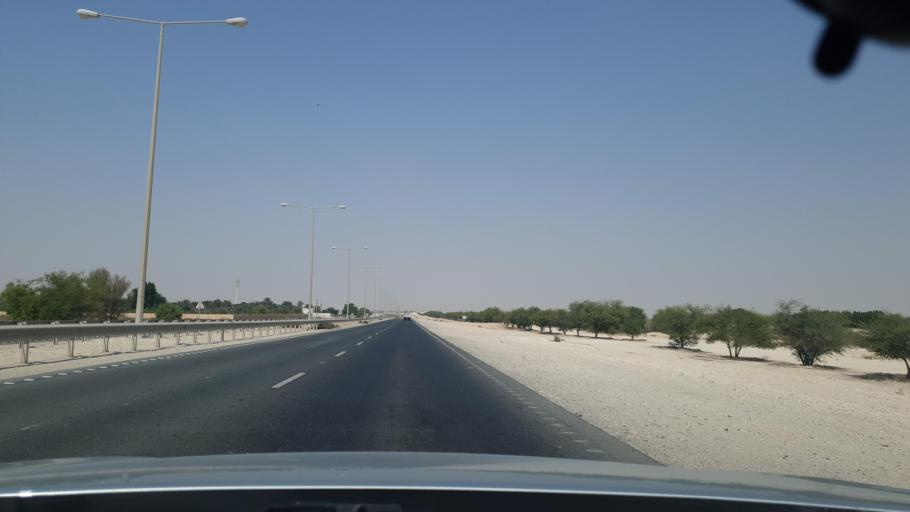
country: QA
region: Al Khawr
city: Al Khawr
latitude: 25.7255
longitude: 51.4970
